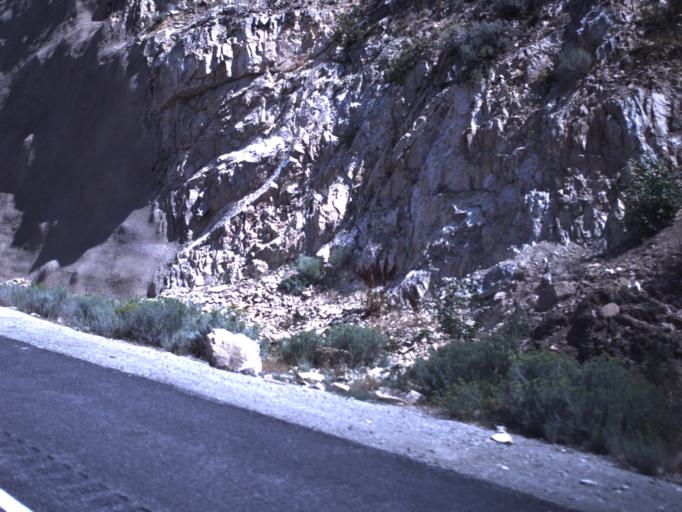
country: US
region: Utah
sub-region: Wasatch County
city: Midway
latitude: 40.4057
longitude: -111.5234
